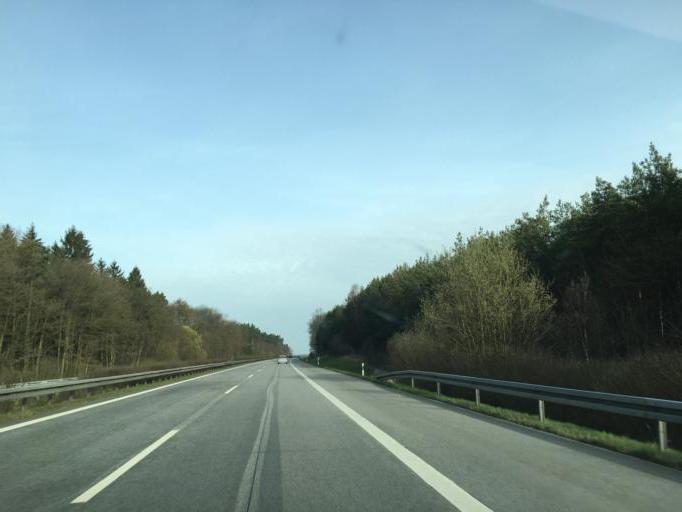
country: DE
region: Mecklenburg-Vorpommern
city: Malchow
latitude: 53.4195
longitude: 12.4302
